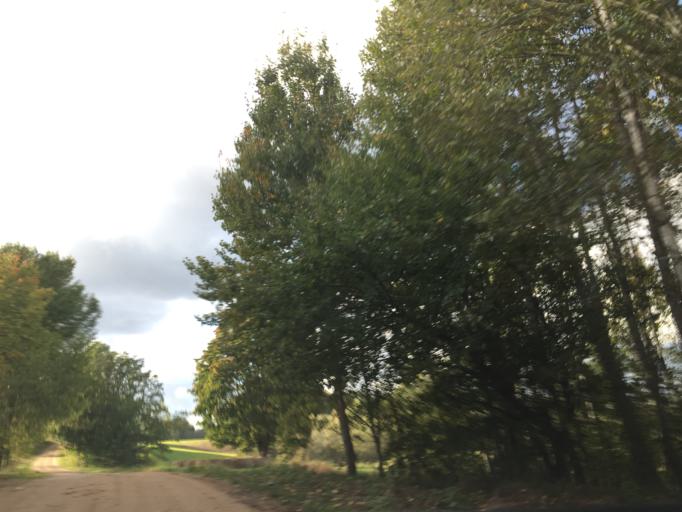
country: LV
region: Ligatne
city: Ligatne
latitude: 57.1365
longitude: 25.0908
